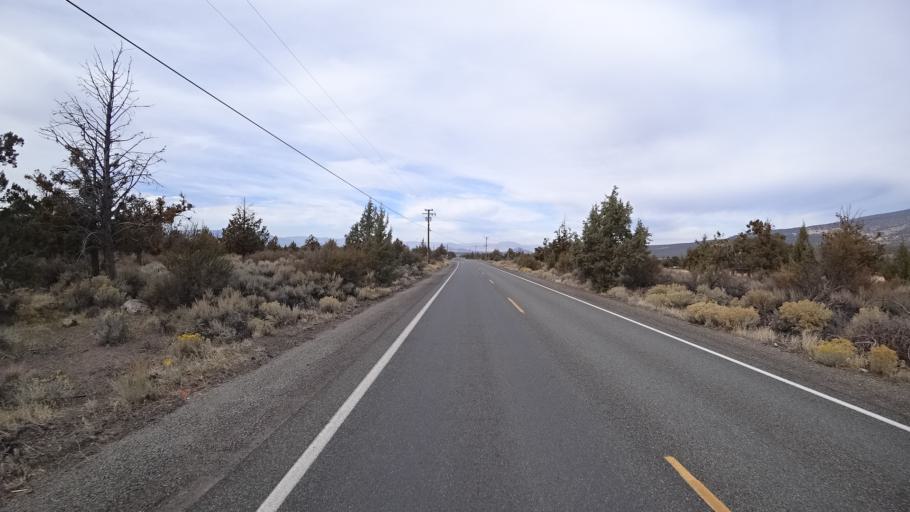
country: US
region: California
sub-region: Siskiyou County
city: Weed
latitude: 41.5786
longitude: -122.2863
